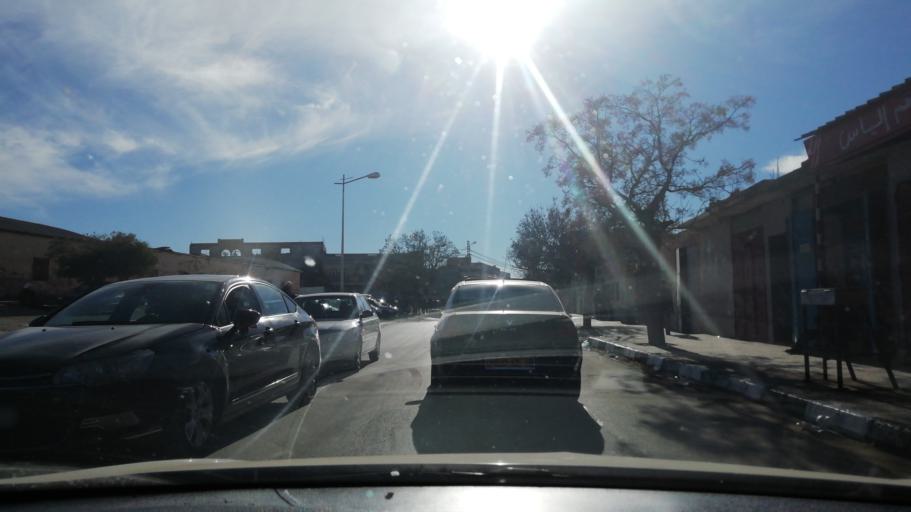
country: DZ
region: Tlemcen
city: Sebdou
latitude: 34.6473
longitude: -1.3220
